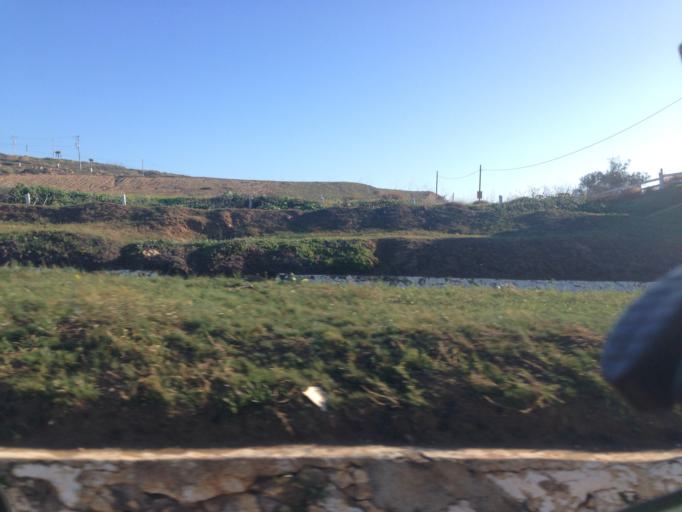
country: MX
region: Baja California
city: Primo Tapia
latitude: 32.2355
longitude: -116.9253
